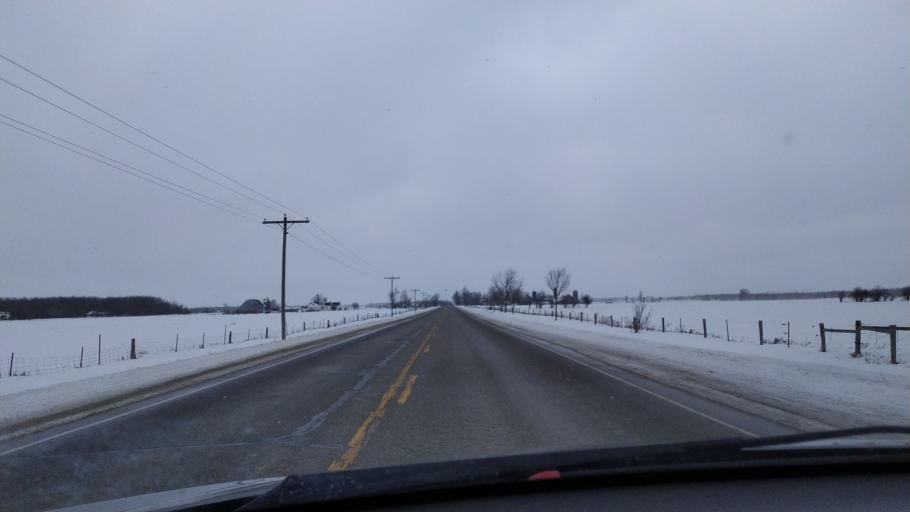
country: CA
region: Ontario
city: North Perth
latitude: 43.5776
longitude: -80.8488
